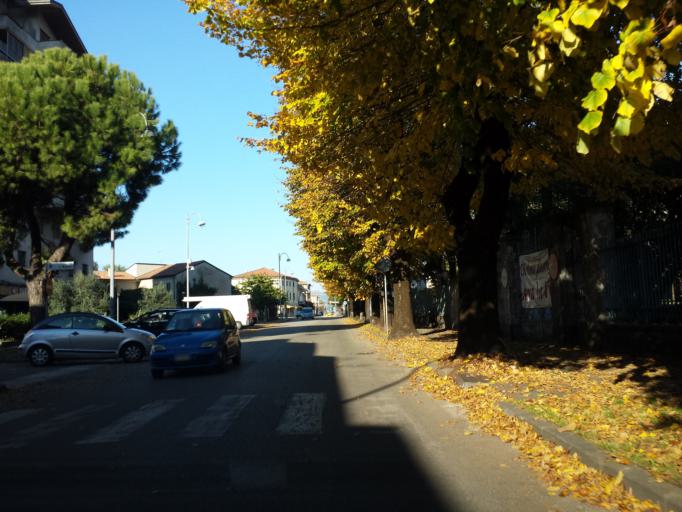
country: IT
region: Veneto
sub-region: Provincia di Verona
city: San Bonifacio
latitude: 45.3988
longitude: 11.2750
